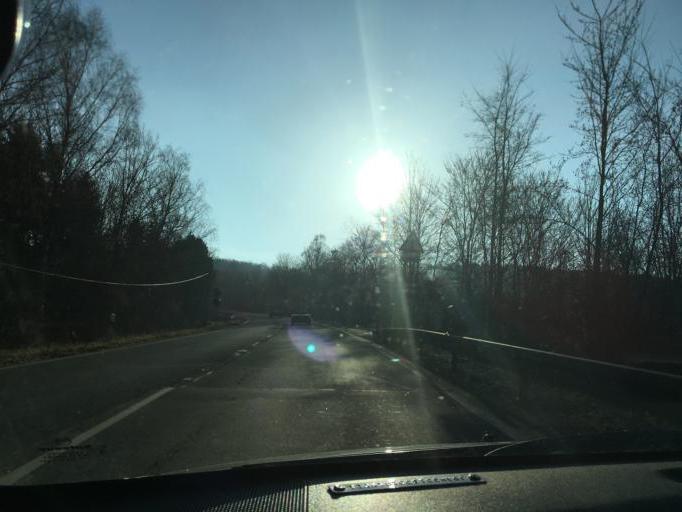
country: DE
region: North Rhine-Westphalia
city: Schwerte
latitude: 51.4316
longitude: 7.6072
